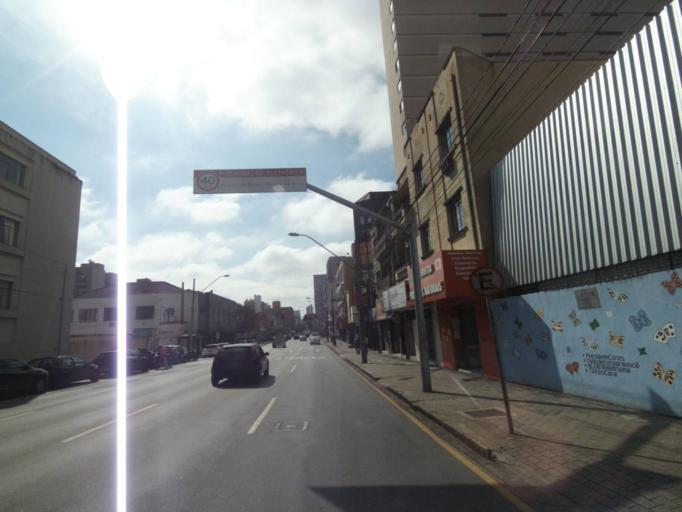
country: BR
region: Parana
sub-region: Curitiba
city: Curitiba
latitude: -25.4342
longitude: -49.2670
